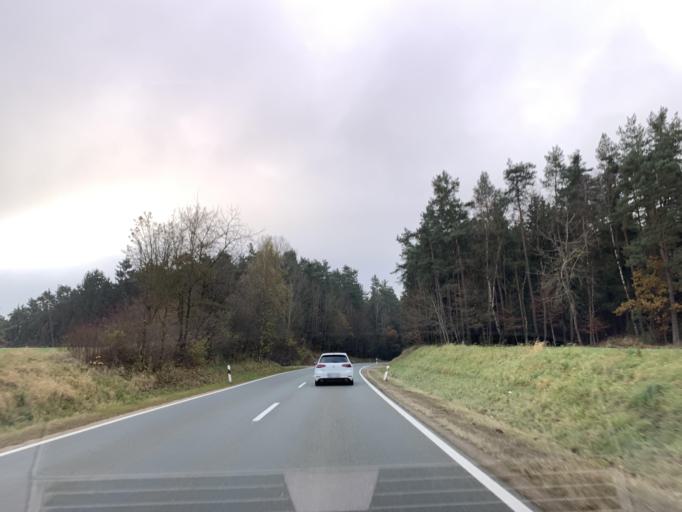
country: DE
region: Bavaria
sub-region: Upper Palatinate
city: Neunburg vorm Wald
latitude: 49.3414
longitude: 12.4239
